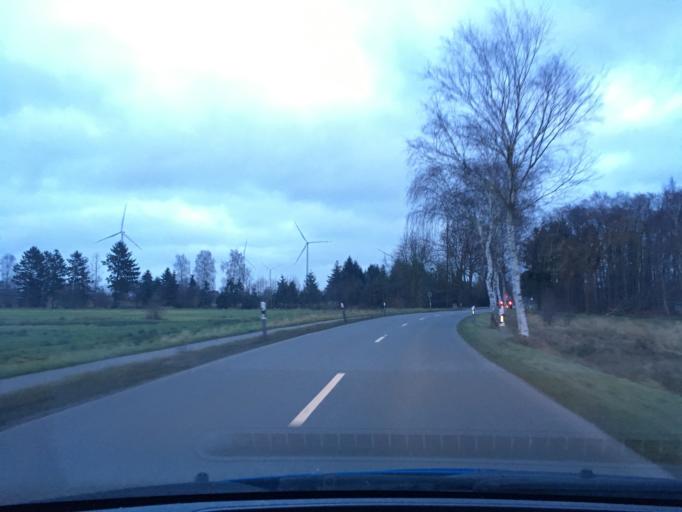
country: DE
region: Lower Saxony
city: Mechtersen
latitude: 53.3030
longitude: 10.3238
